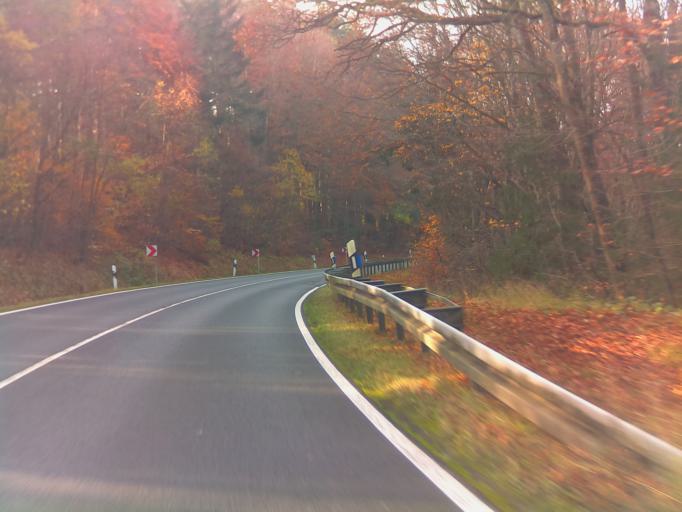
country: DE
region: Bavaria
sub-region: Regierungsbezirk Unterfranken
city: Bad Bocklet
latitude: 50.2519
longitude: 10.0393
